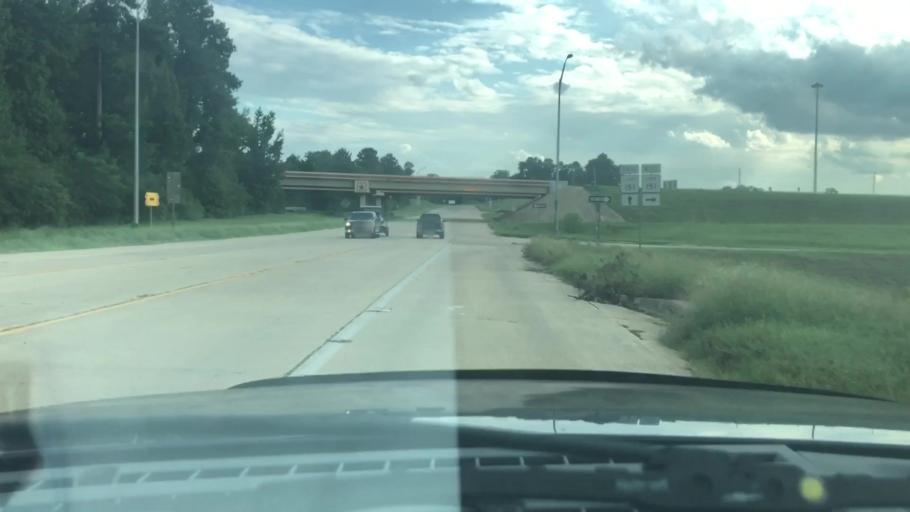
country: US
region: Texas
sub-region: Bowie County
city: Texarkana
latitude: 33.3875
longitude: -94.0662
